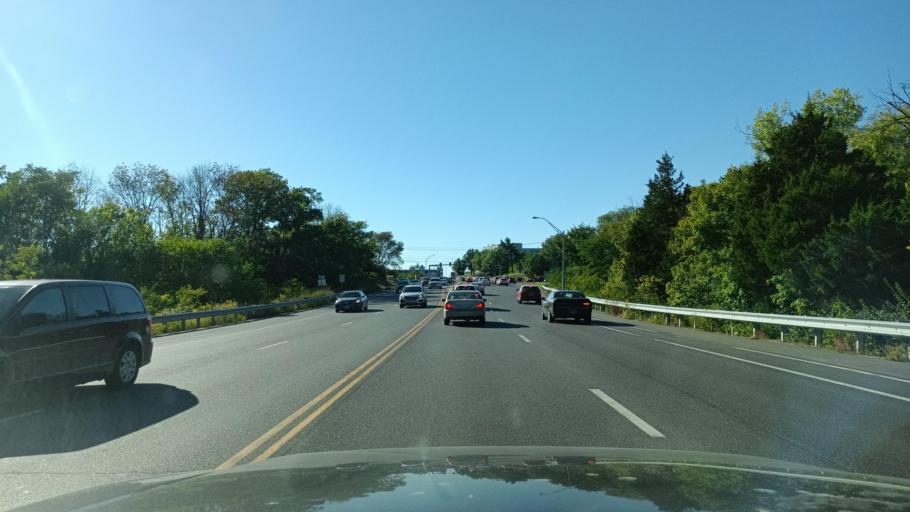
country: US
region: Missouri
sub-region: Boone County
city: Columbia
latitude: 38.9341
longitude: -92.3204
